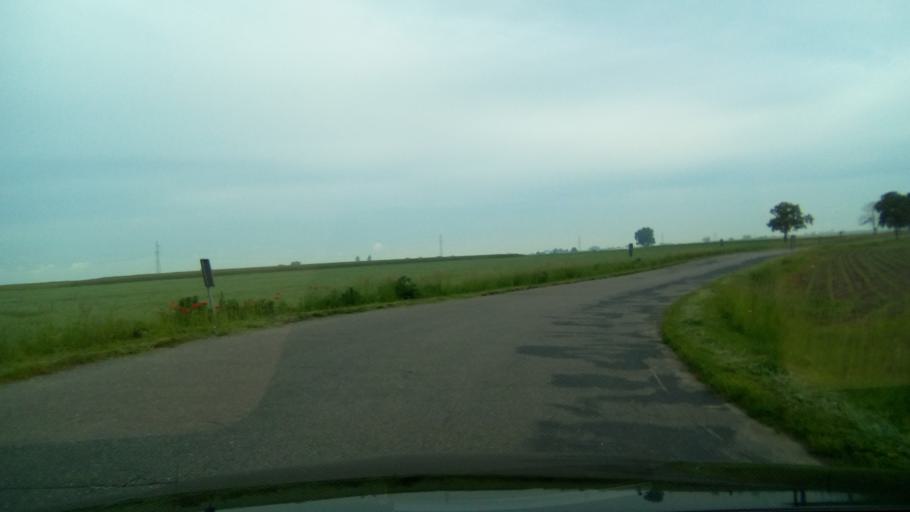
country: PL
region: Greater Poland Voivodeship
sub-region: Powiat gnieznienski
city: Mieleszyn
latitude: 52.6204
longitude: 17.5334
